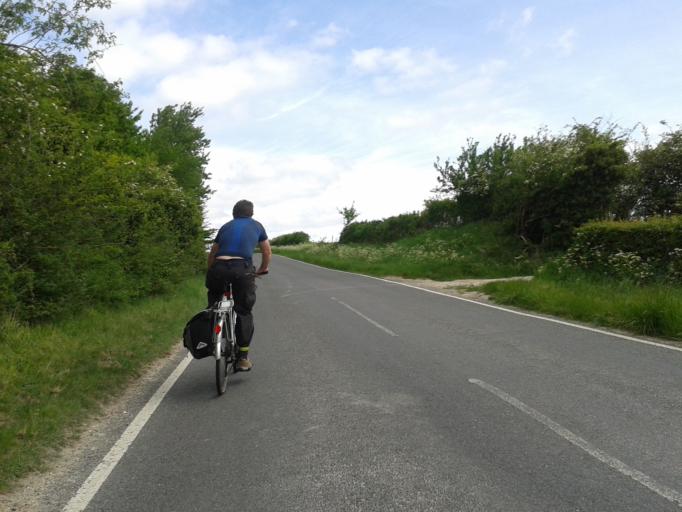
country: GB
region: England
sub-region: Cambridgeshire
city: Haslingfield
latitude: 52.1405
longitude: 0.0440
